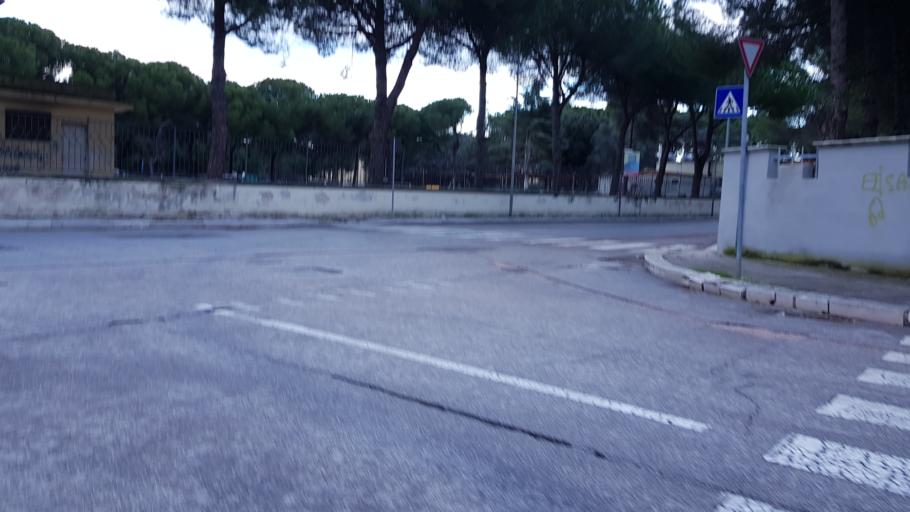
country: IT
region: Apulia
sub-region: Provincia di Brindisi
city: Brindisi
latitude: 40.6192
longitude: 17.9189
